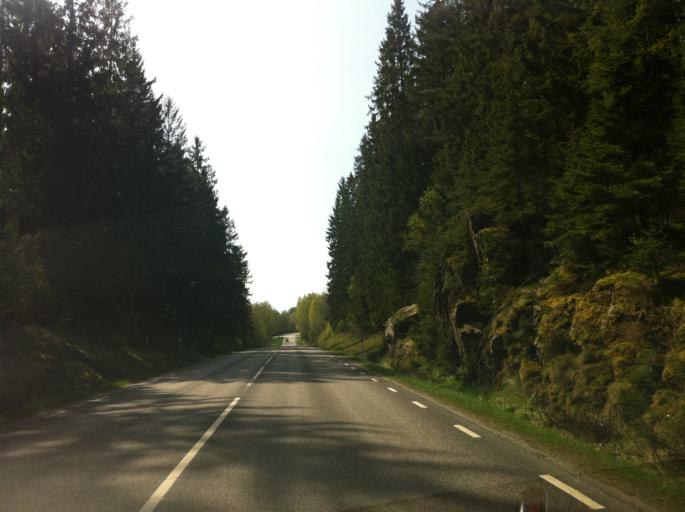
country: SE
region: Vaestra Goetaland
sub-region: Marks Kommun
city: Fritsla
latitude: 57.3305
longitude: 12.8952
